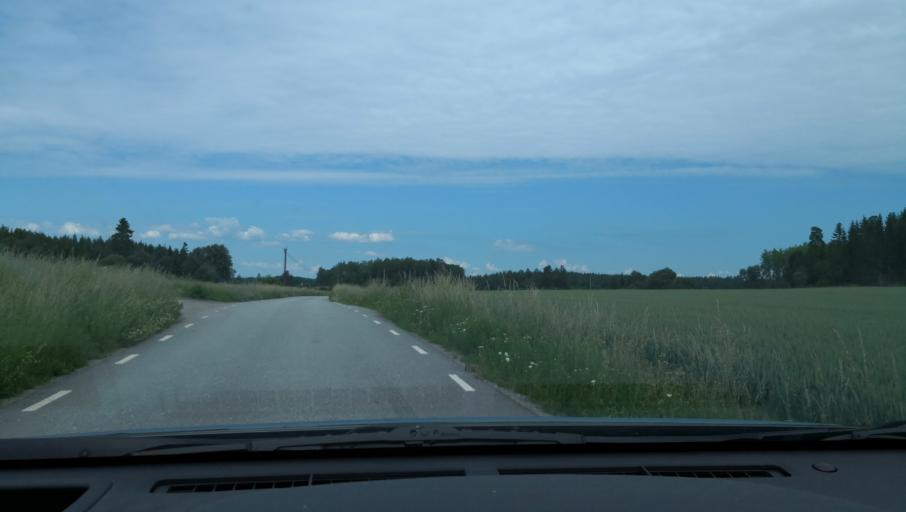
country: SE
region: Uppsala
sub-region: Habo Kommun
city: Balsta
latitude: 59.7051
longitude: 17.4760
